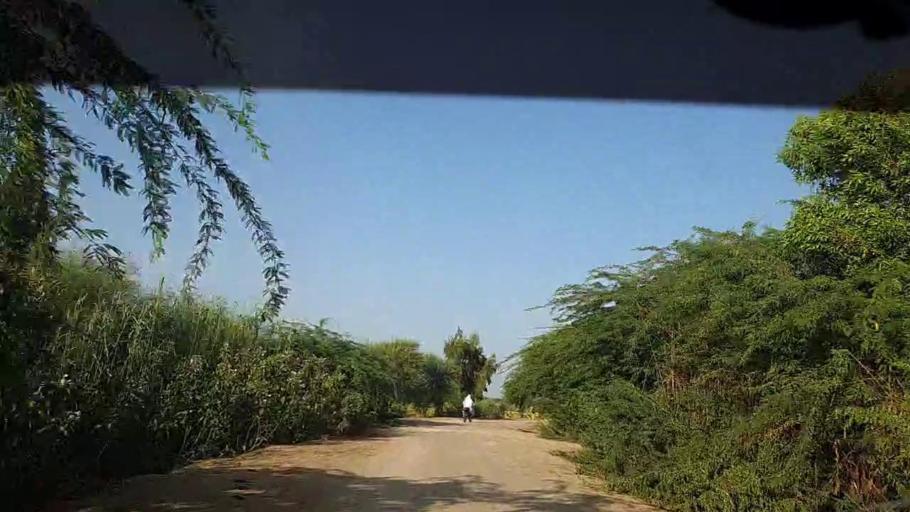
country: PK
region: Sindh
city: Badin
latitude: 24.6987
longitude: 68.8617
